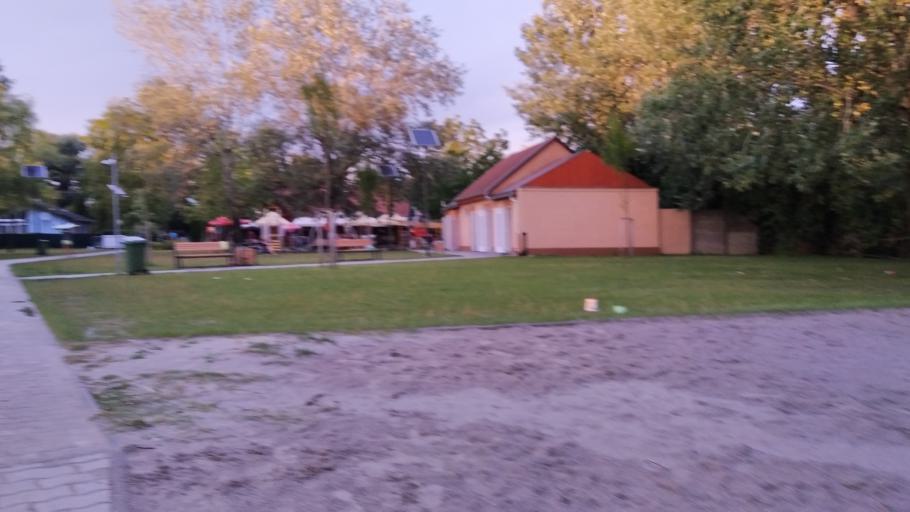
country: HU
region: Veszprem
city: Balatonkenese
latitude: 47.0259
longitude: 18.1264
